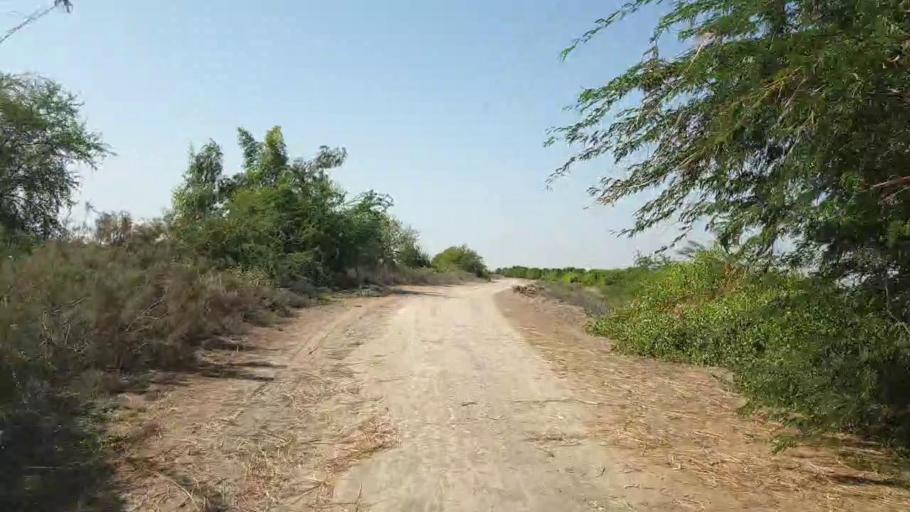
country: PK
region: Sindh
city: Tando Bago
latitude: 24.7049
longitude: 69.0222
